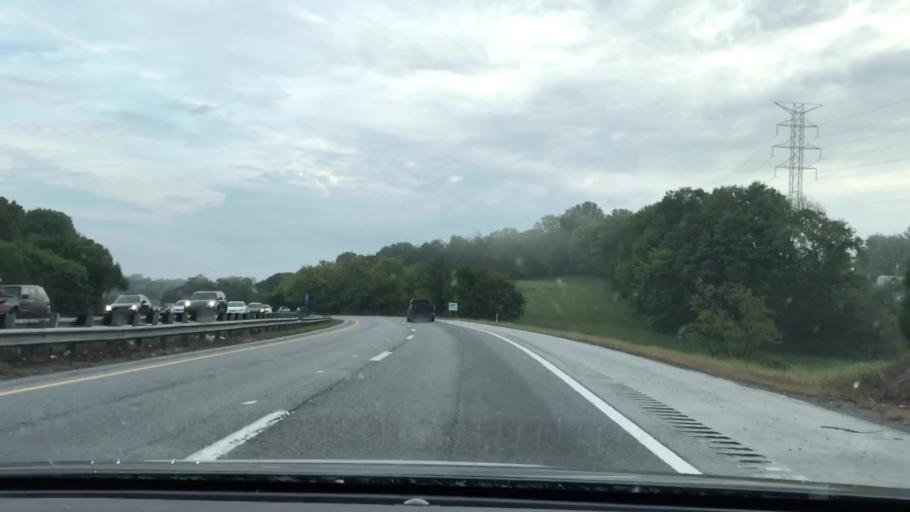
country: US
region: Tennessee
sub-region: Sumner County
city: Hendersonville
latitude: 36.3197
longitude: -86.6392
